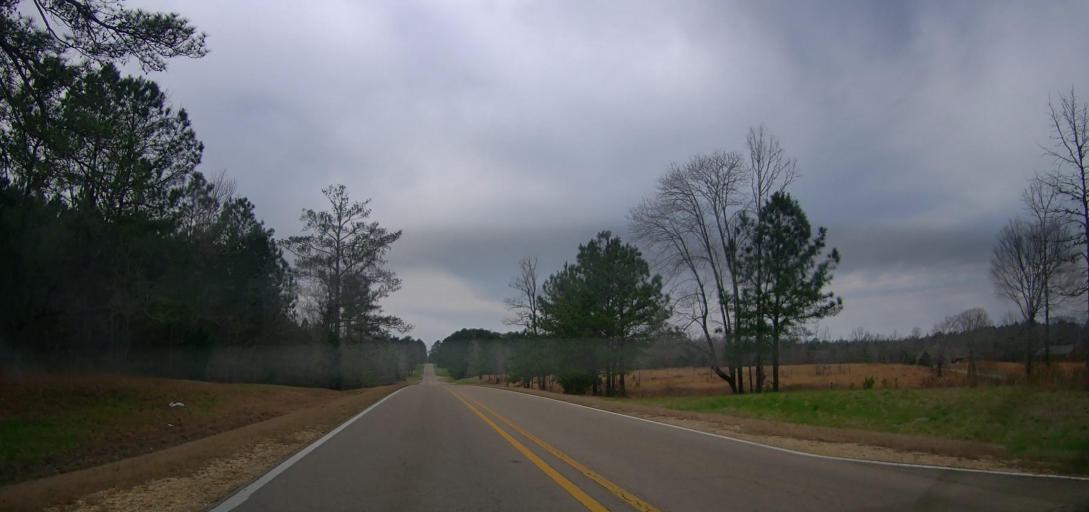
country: US
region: Mississippi
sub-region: Itawamba County
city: Mantachie
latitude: 34.2625
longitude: -88.5317
